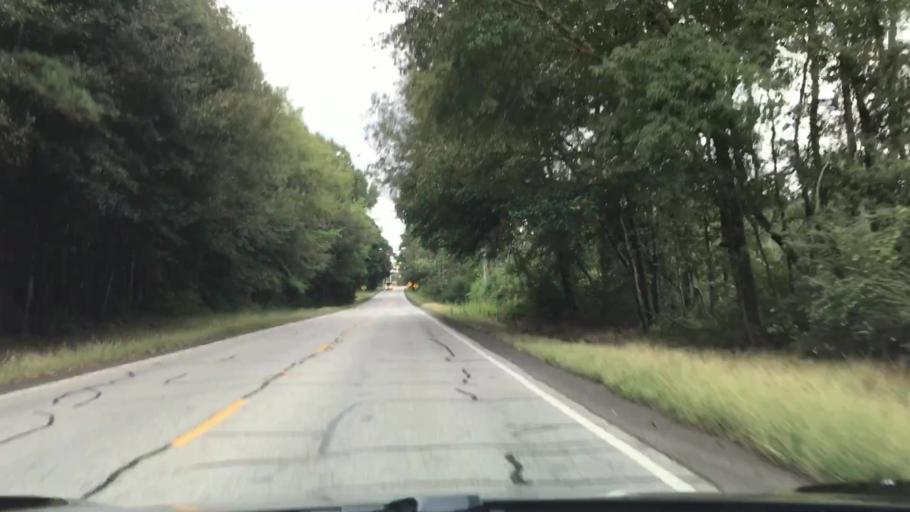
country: US
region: Georgia
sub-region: Barrow County
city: Russell
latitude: 33.9583
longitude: -83.6611
